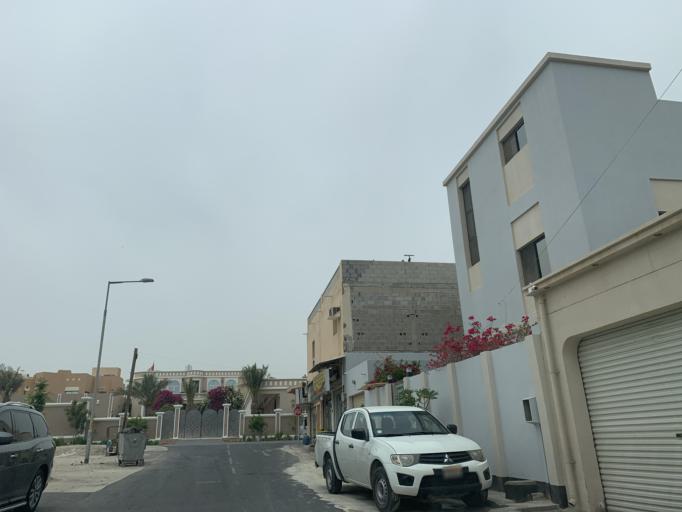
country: BH
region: Northern
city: Ar Rifa'
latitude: 26.1369
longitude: 50.5522
